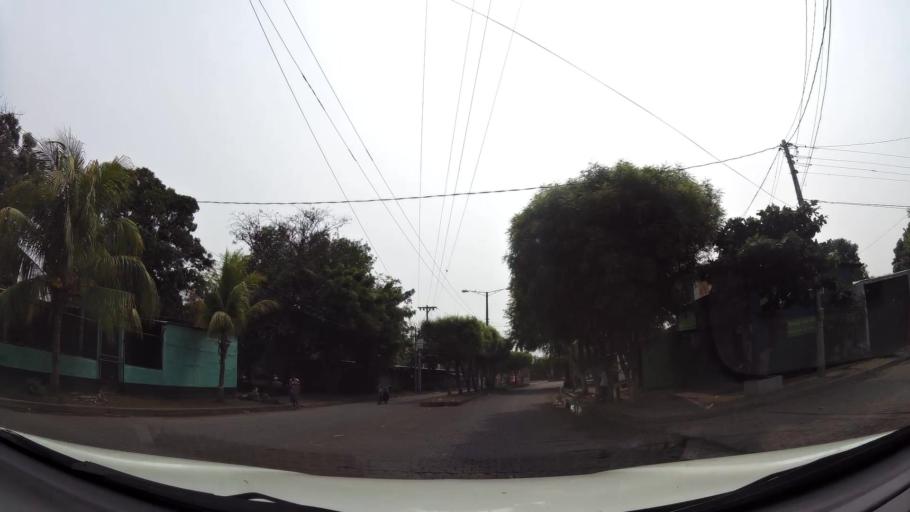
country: NI
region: Chinandega
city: Chinandega
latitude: 12.6279
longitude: -87.1419
